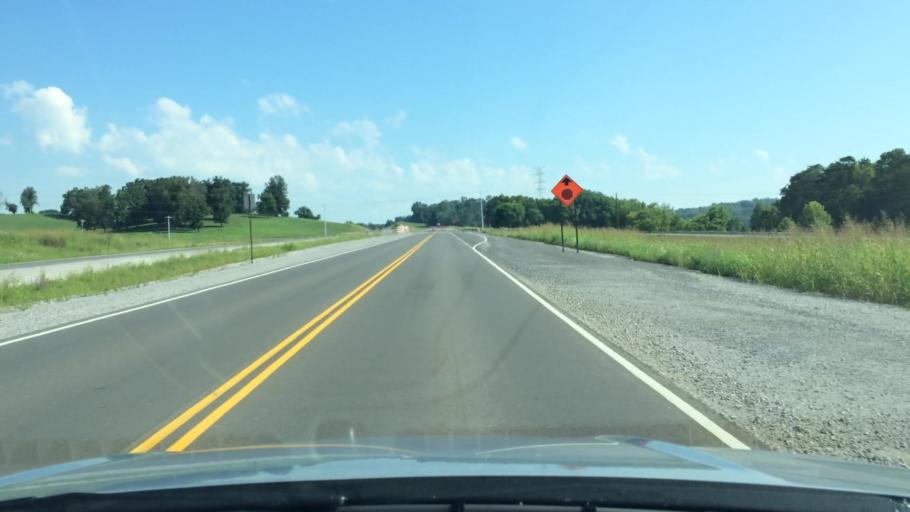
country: US
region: Tennessee
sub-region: Jefferson County
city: White Pine
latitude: 36.1461
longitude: -83.3433
